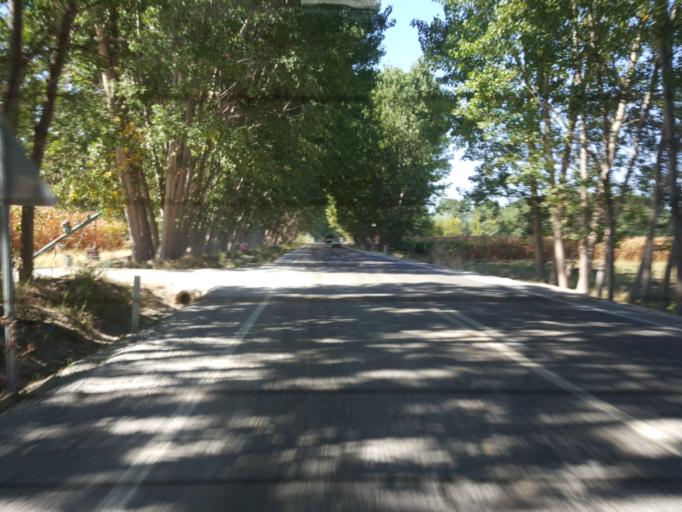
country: TR
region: Tokat
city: Pazar
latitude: 40.2687
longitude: 36.2158
